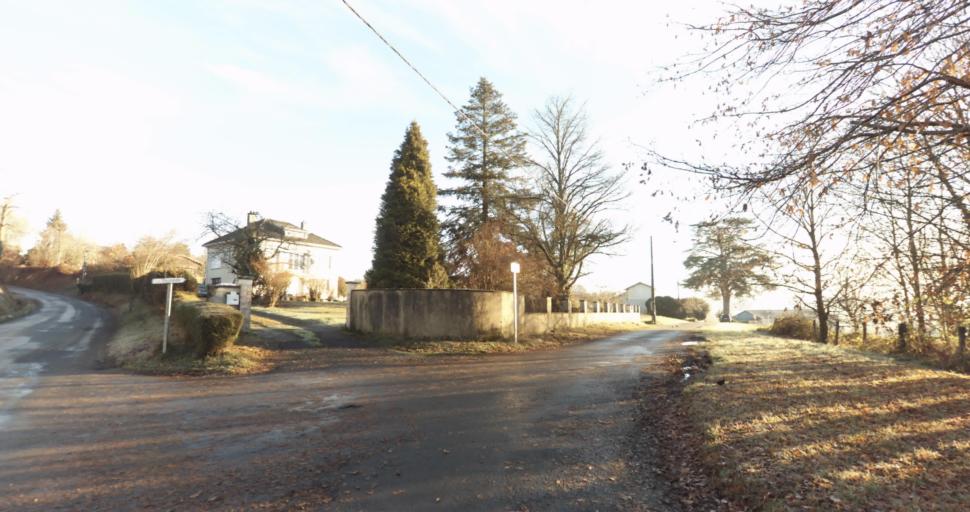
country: FR
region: Limousin
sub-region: Departement de la Haute-Vienne
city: Aixe-sur-Vienne
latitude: 45.8120
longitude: 1.1495
